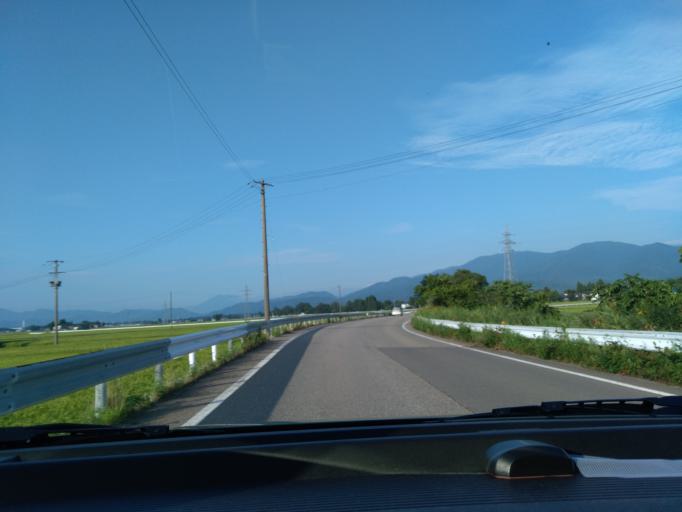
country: JP
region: Akita
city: Kakunodatemachi
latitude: 39.5556
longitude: 140.5667
